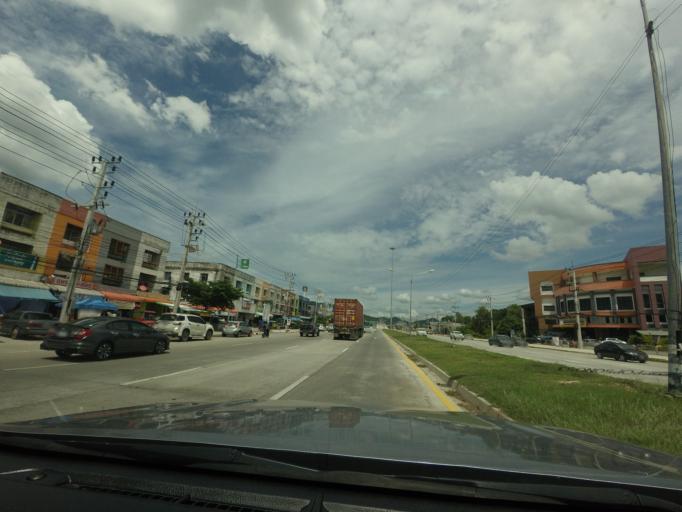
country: TH
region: Songkhla
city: Songkhla
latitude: 7.1369
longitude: 100.5732
